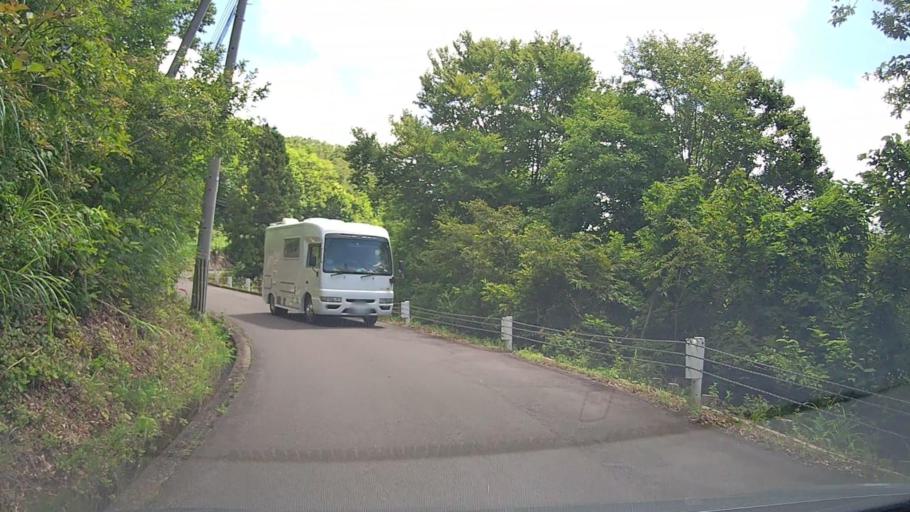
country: JP
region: Nagano
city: Iiyama
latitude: 36.9351
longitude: 138.4631
